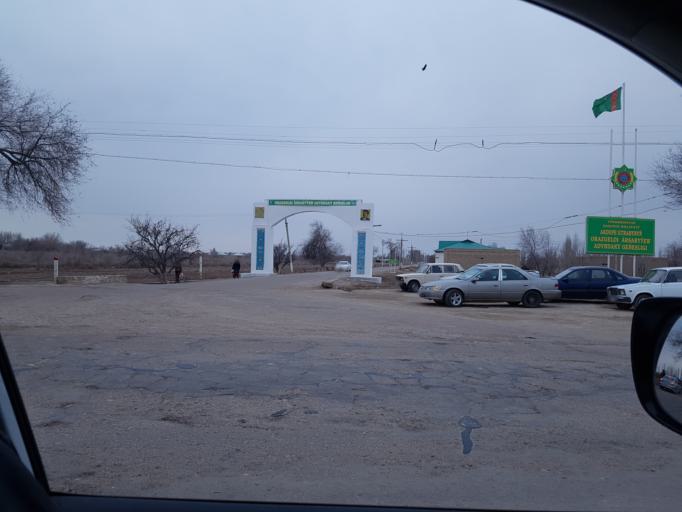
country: TM
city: Akdepe
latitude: 41.9971
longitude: 59.4417
